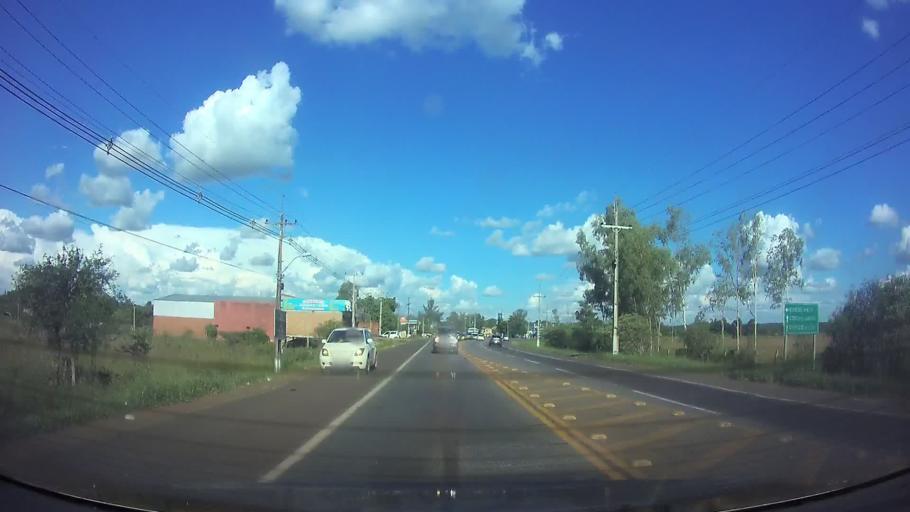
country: PY
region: Cordillera
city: Eusebio Ayala
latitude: -25.3820
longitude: -56.9744
